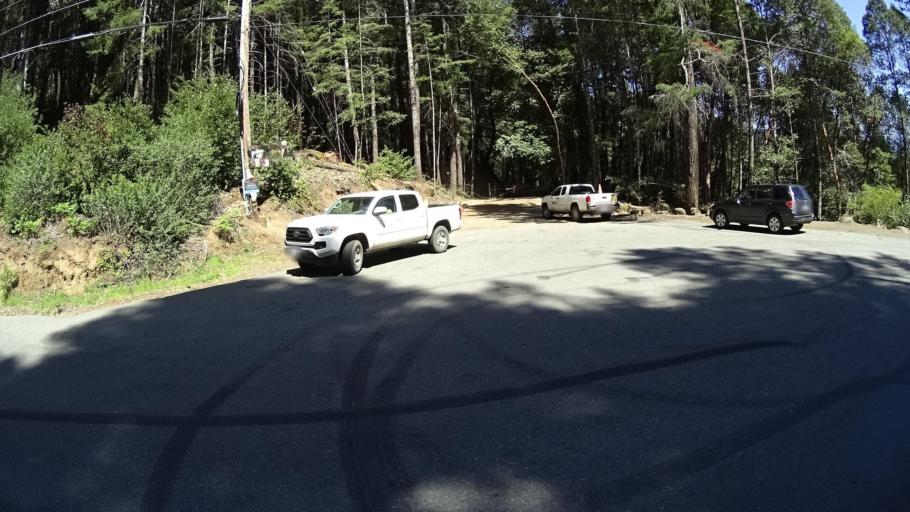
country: US
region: California
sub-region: Humboldt County
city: Redway
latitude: 40.0887
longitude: -123.9445
